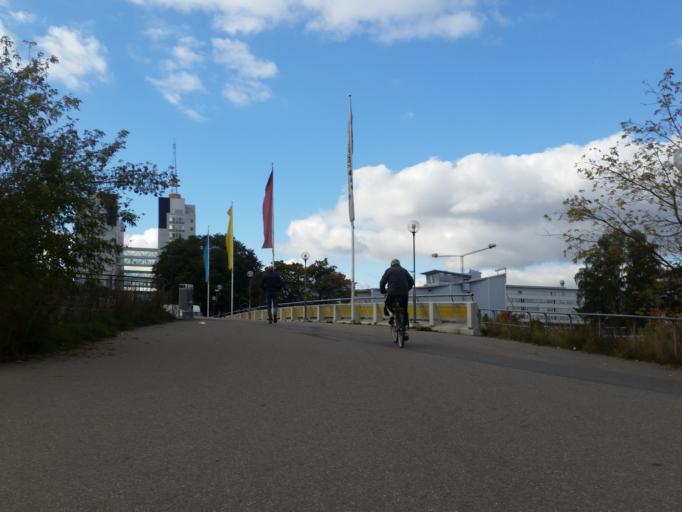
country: SE
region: Stockholm
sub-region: Stockholms Kommun
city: Arsta
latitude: 59.2945
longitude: 18.0857
